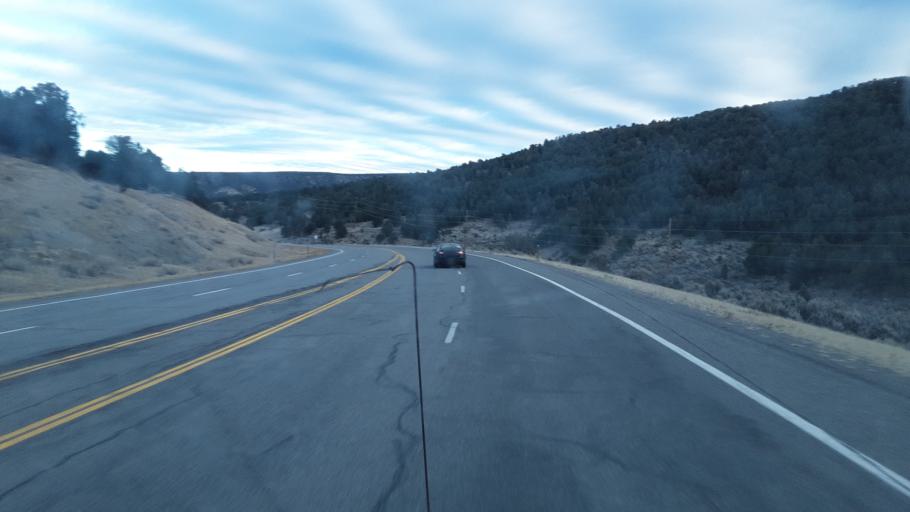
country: US
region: Colorado
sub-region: Ouray County
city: Ouray
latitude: 38.2113
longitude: -107.7272
